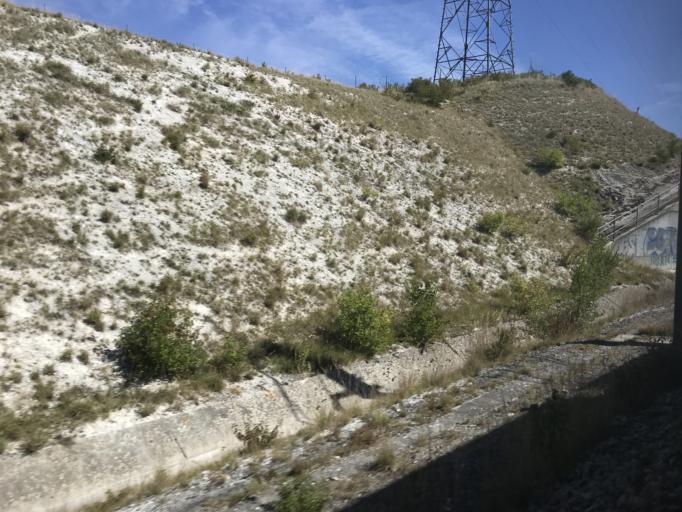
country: FR
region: Champagne-Ardenne
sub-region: Departement de la Marne
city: Cormontreuil
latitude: 49.2065
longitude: 4.0281
